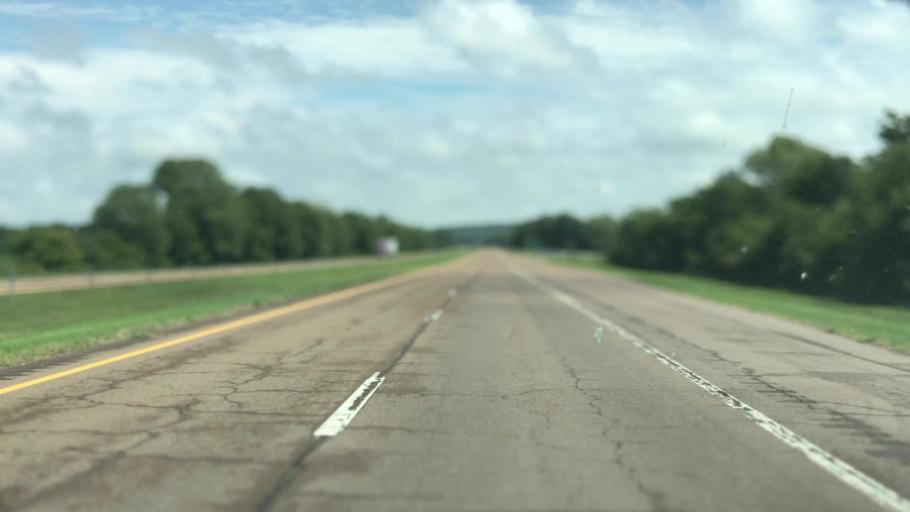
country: US
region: Tennessee
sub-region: Dyer County
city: Dyersburg
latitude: 36.0805
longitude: -89.5284
